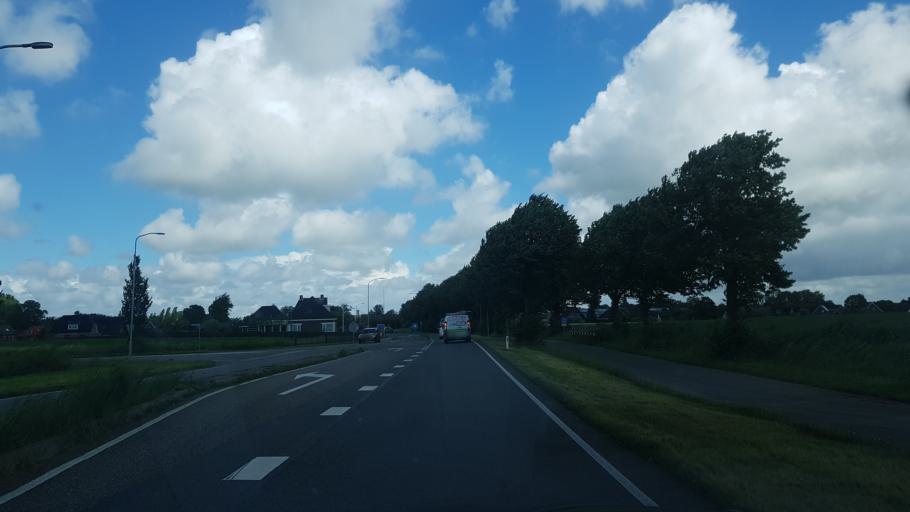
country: NL
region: Groningen
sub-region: Gemeente Winsum
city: Winsum
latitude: 53.3902
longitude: 6.5463
